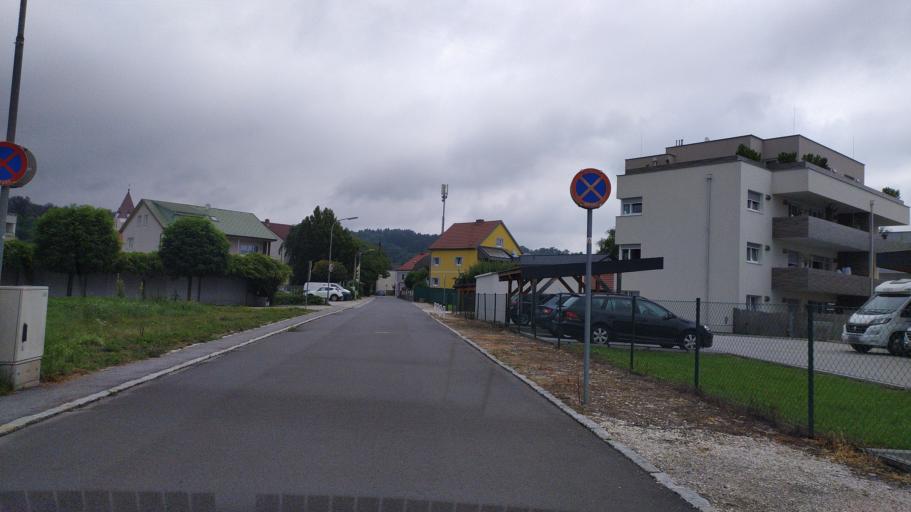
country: AT
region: Upper Austria
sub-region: Politischer Bezirk Perg
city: Perg
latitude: 48.2470
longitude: 14.6327
